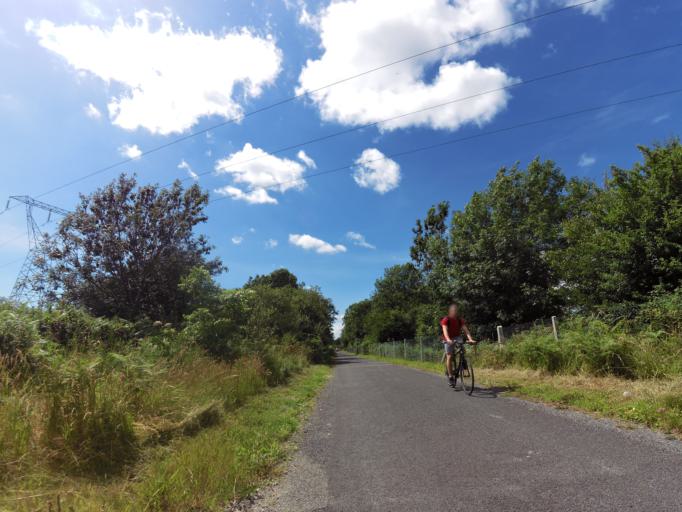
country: IE
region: Munster
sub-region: Waterford
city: Portlaw
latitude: 52.2384
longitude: -7.2877
